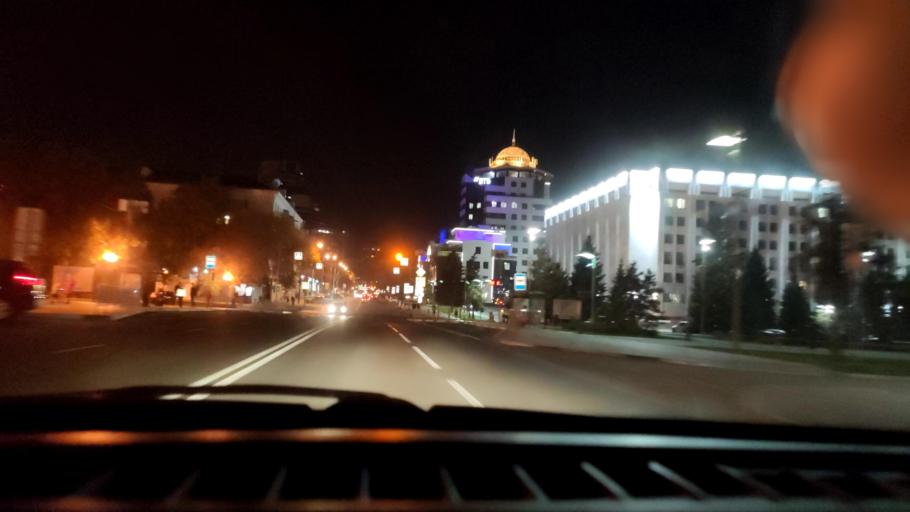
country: RU
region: Samara
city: Samara
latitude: 53.2029
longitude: 50.1119
